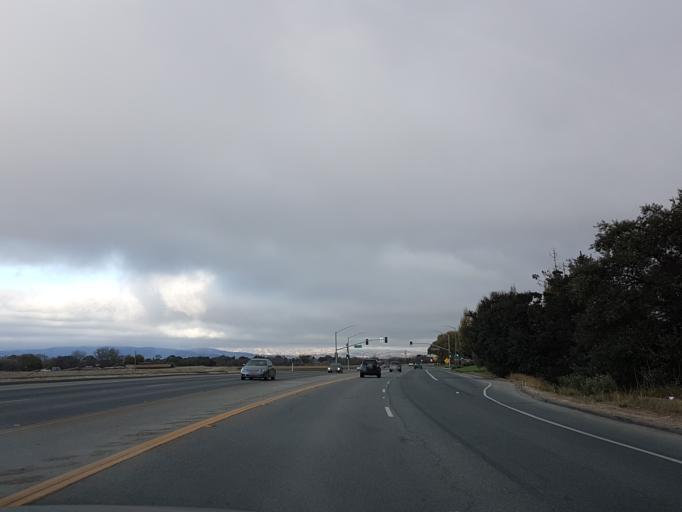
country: US
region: California
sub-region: Monterey County
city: Salinas
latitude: 36.6225
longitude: -121.6713
